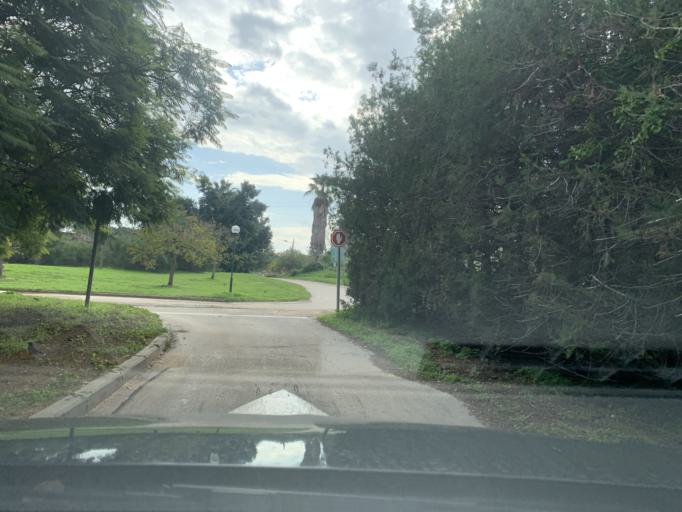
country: PS
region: West Bank
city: Qalqilyah
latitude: 32.1981
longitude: 34.9467
